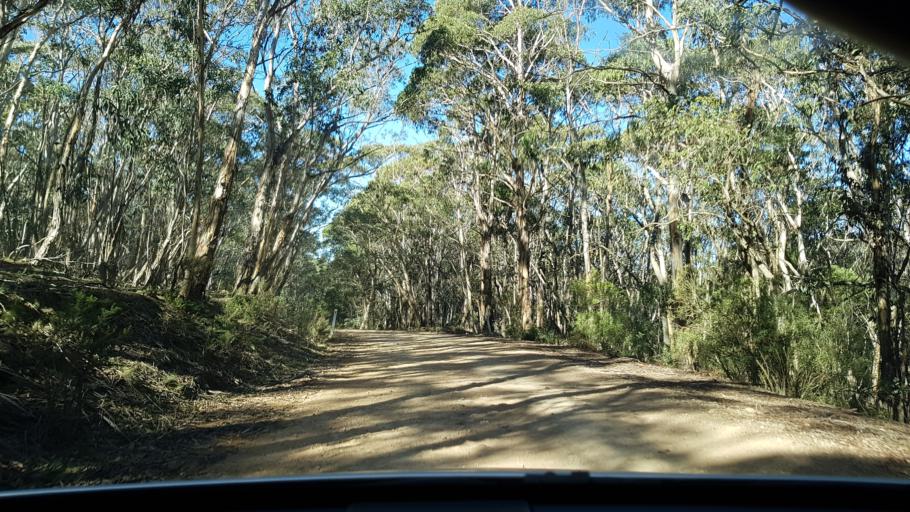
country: AU
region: New South Wales
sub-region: Oberon
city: Oberon
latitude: -33.8489
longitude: 150.0202
